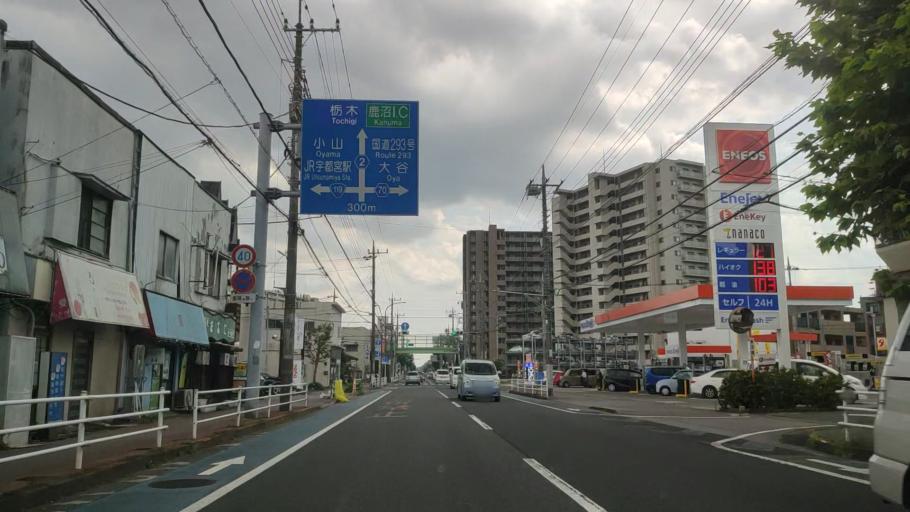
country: JP
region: Tochigi
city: Utsunomiya-shi
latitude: 36.5685
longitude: 139.8689
